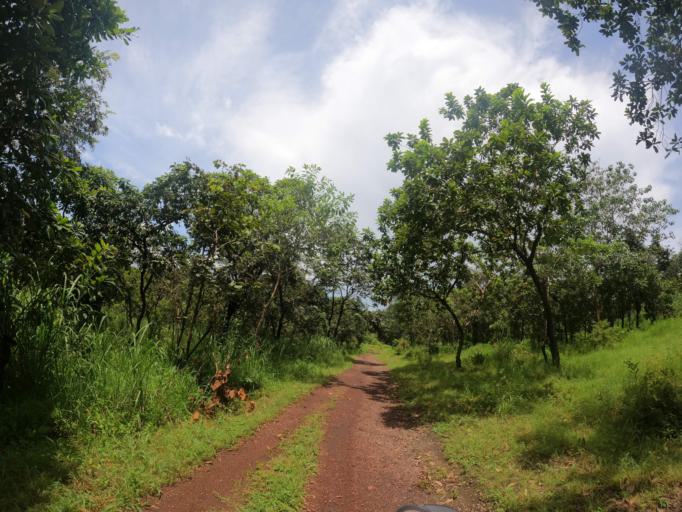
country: SL
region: Northern Province
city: Binkolo
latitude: 9.1605
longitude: -12.1884
